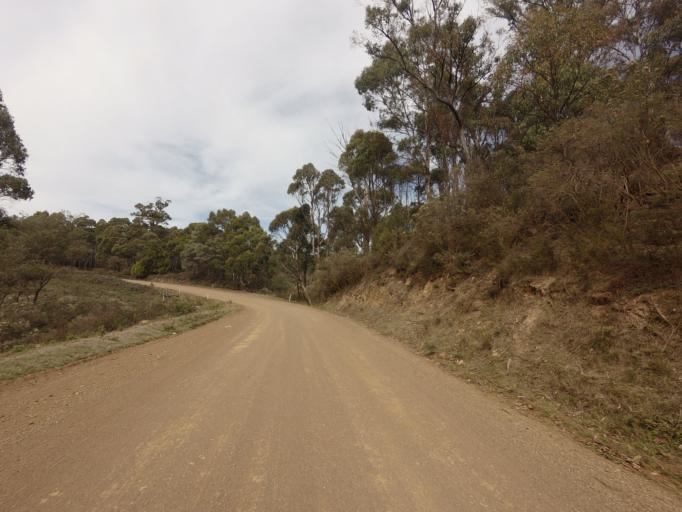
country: AU
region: Tasmania
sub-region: Sorell
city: Sorell
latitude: -42.4992
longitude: 147.6309
